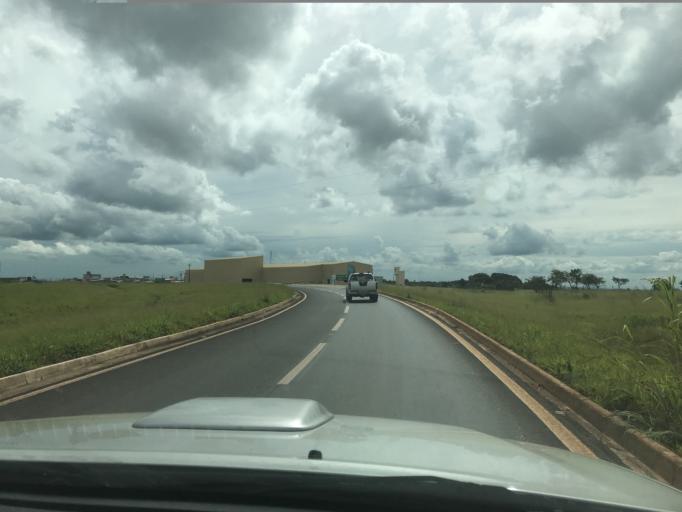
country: BR
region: Minas Gerais
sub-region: Patrocinio
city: Patrocinio
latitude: -19.0963
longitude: -46.6713
